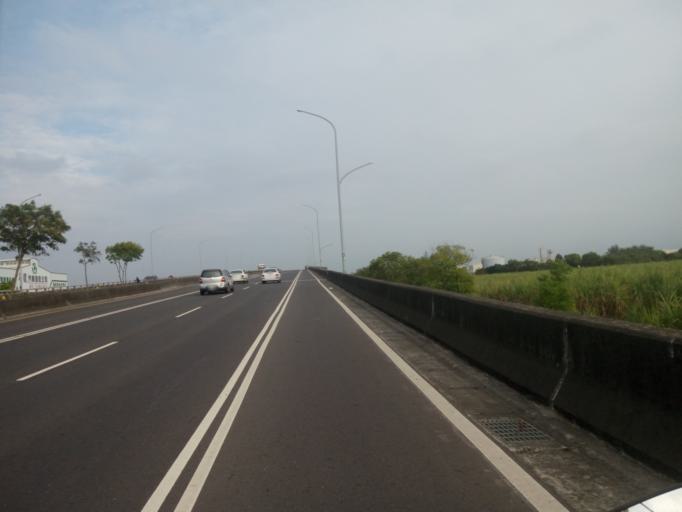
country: TW
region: Taiwan
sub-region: Chiayi
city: Taibao
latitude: 23.4863
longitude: 120.3825
